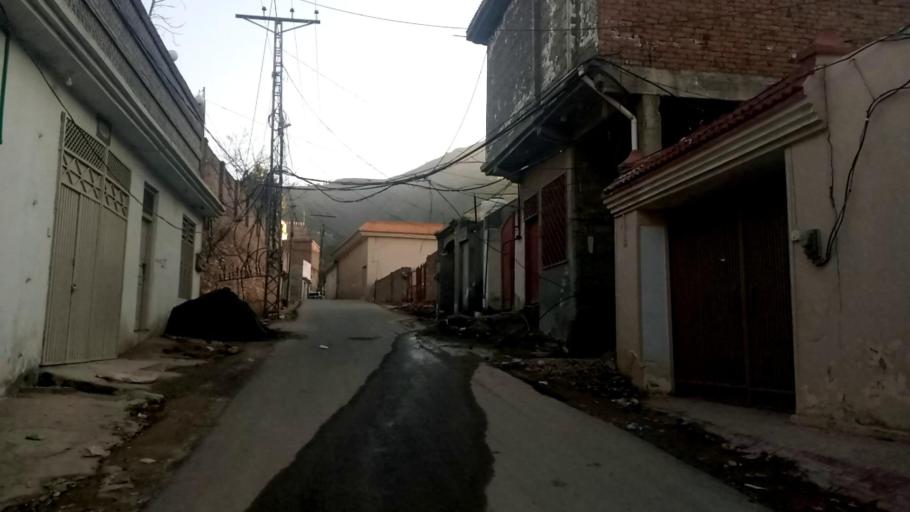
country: PK
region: Khyber Pakhtunkhwa
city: Saidu Sharif
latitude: 34.7419
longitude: 72.3515
